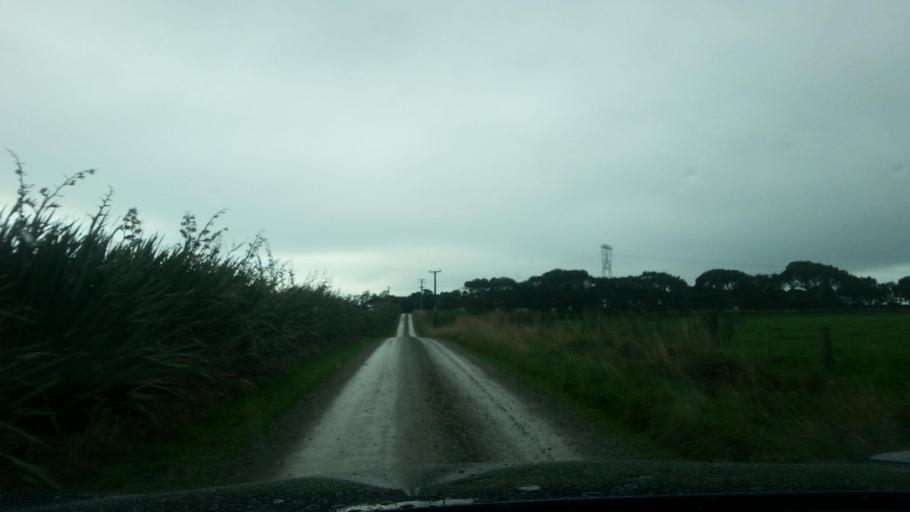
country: NZ
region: Southland
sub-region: Invercargill City
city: Invercargill
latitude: -46.3310
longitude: 168.4466
